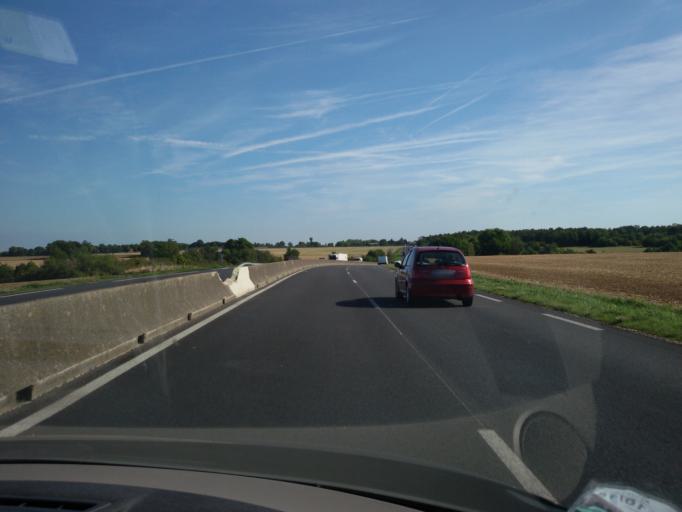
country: FR
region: Ile-de-France
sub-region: Departement de l'Essonne
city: Mereville
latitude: 48.3628
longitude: 2.0656
